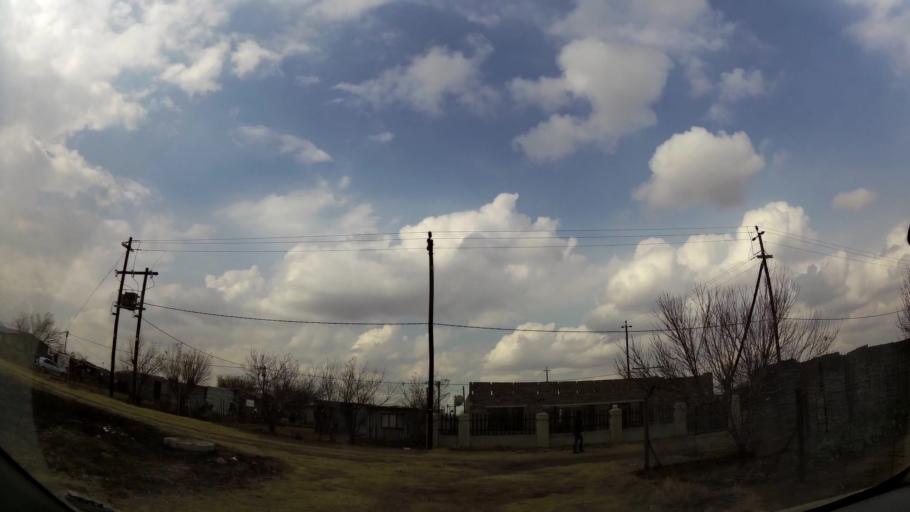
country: ZA
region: Orange Free State
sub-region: Fezile Dabi District Municipality
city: Sasolburg
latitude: -26.8642
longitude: 27.8988
